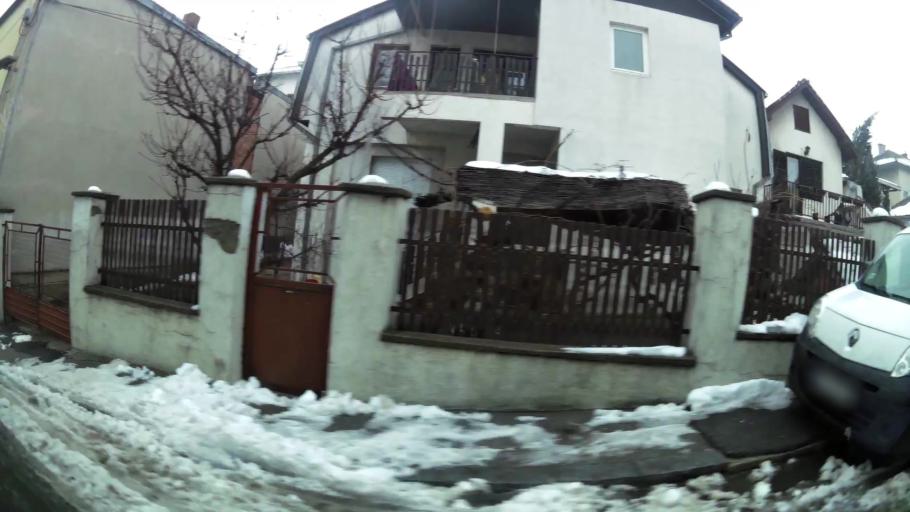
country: RS
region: Central Serbia
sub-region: Belgrade
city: Zvezdara
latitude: 44.7879
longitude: 20.5183
